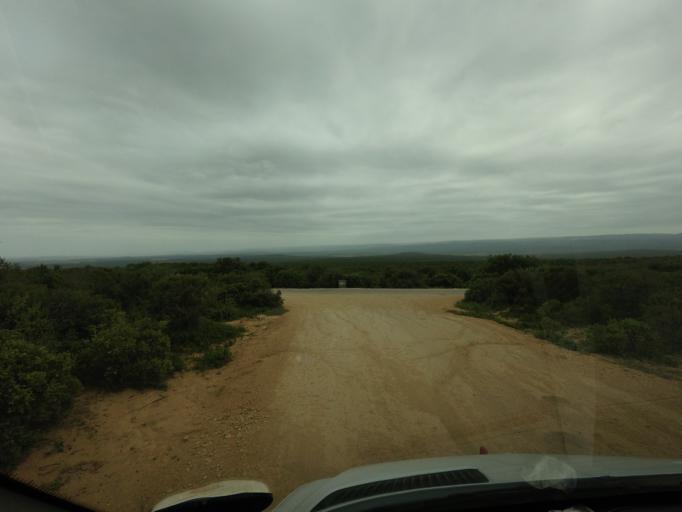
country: ZA
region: Eastern Cape
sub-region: Cacadu District Municipality
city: Kirkwood
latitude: -33.4855
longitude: 25.7557
